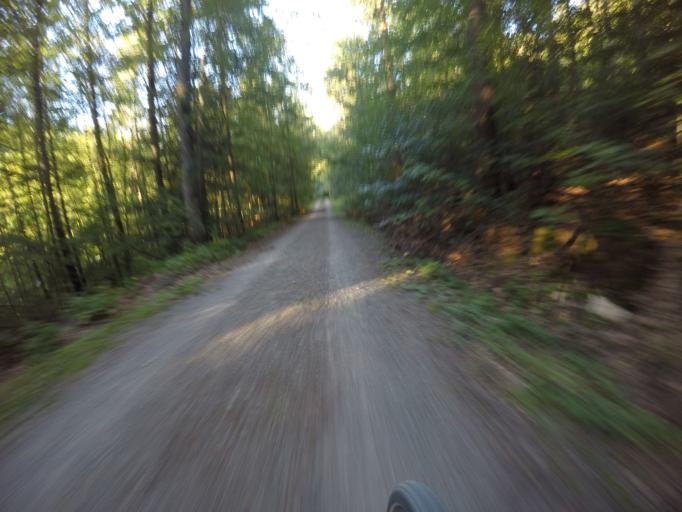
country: DE
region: Baden-Wuerttemberg
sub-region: Regierungsbezirk Stuttgart
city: Waldenbuch
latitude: 48.6409
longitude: 9.1105
